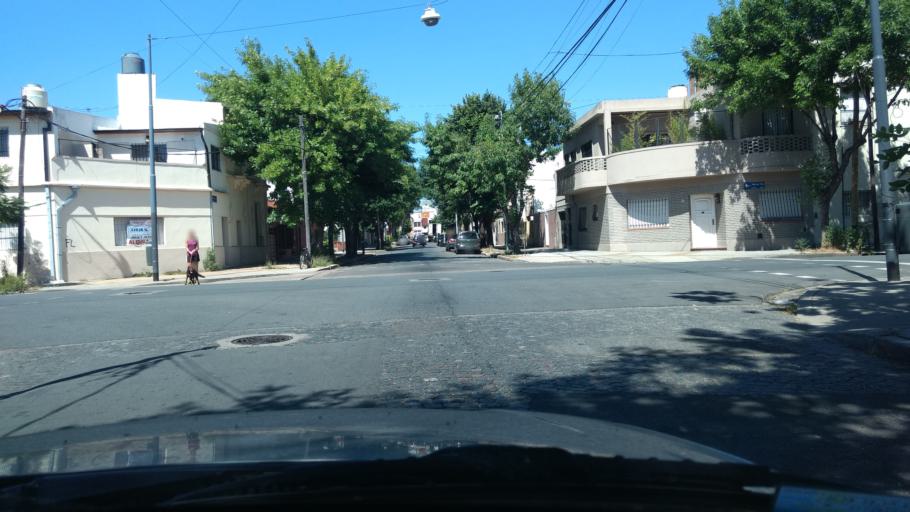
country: AR
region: Buenos Aires F.D.
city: Villa Santa Rita
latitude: -34.6166
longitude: -58.5053
